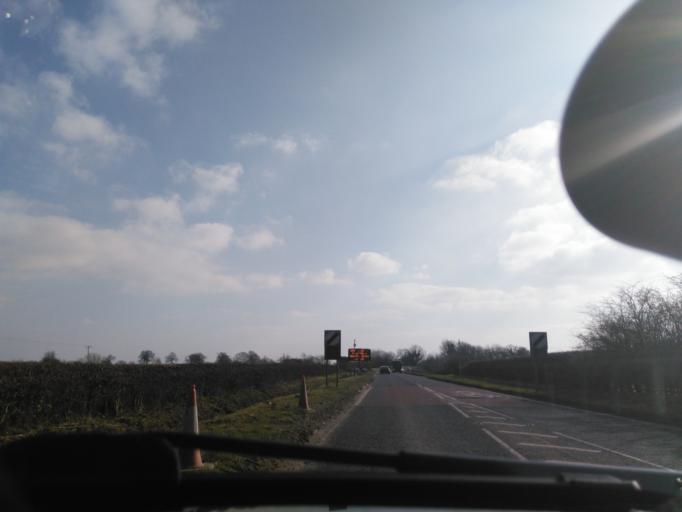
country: GB
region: England
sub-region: Wiltshire
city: Norton
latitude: 51.5239
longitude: -2.1223
